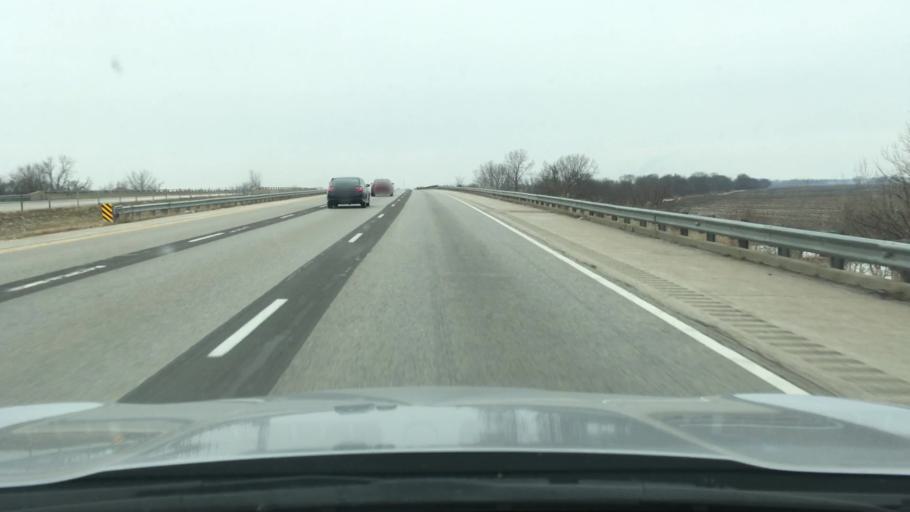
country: US
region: Illinois
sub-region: Sangamon County
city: Divernon
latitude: 39.6285
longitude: -89.6466
